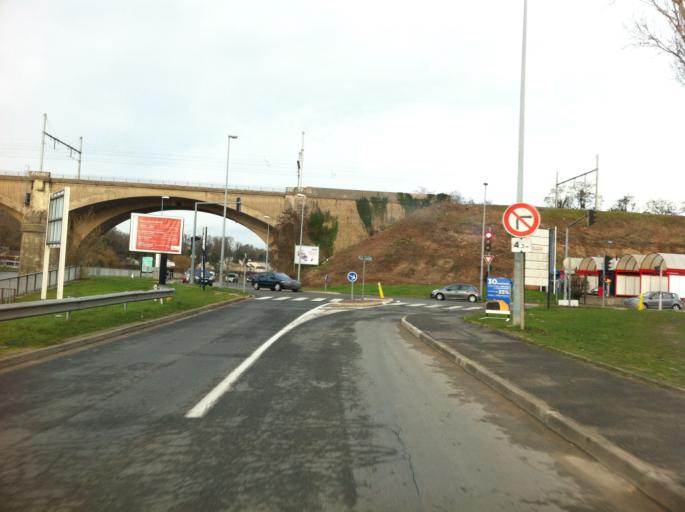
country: FR
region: Ile-de-France
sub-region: Departement de Seine-et-Marne
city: Le Mee-sur-Seine
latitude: 48.5302
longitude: 2.6390
